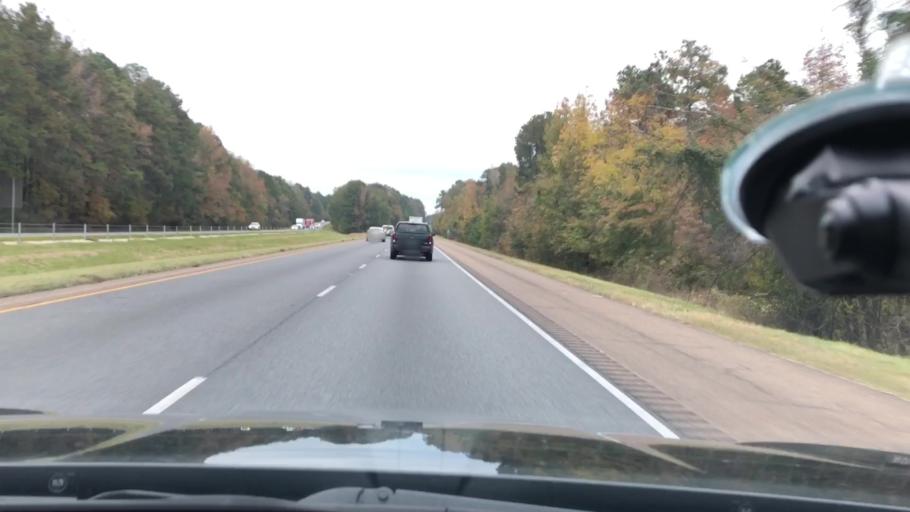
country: US
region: Arkansas
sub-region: Clark County
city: Gurdon
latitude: 33.9151
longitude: -93.2807
